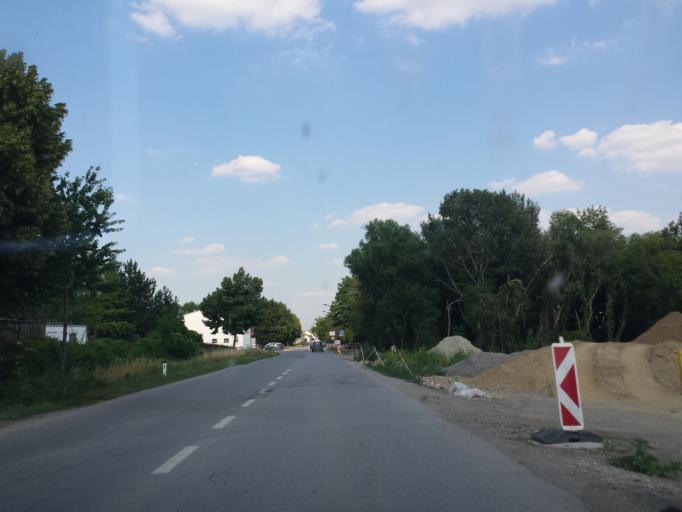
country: AT
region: Lower Austria
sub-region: Politischer Bezirk Ganserndorf
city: Aderklaa
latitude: 48.2837
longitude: 16.5300
